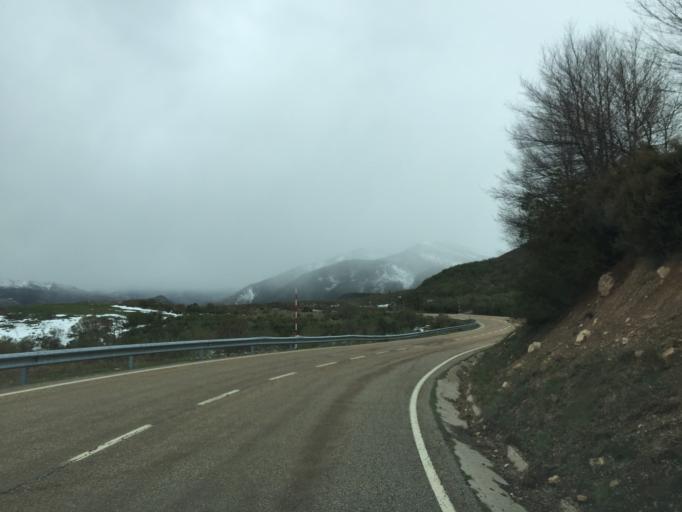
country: ES
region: Castille and Leon
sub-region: Provincia de Leon
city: San Emiliano
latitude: 43.0395
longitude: -6.0134
